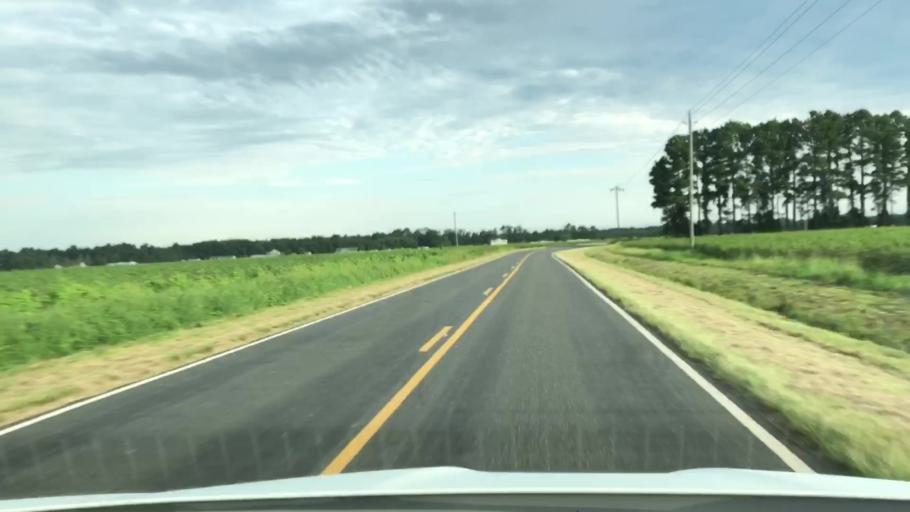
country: US
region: North Carolina
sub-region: Jones County
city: Maysville
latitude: 34.9892
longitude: -77.2801
